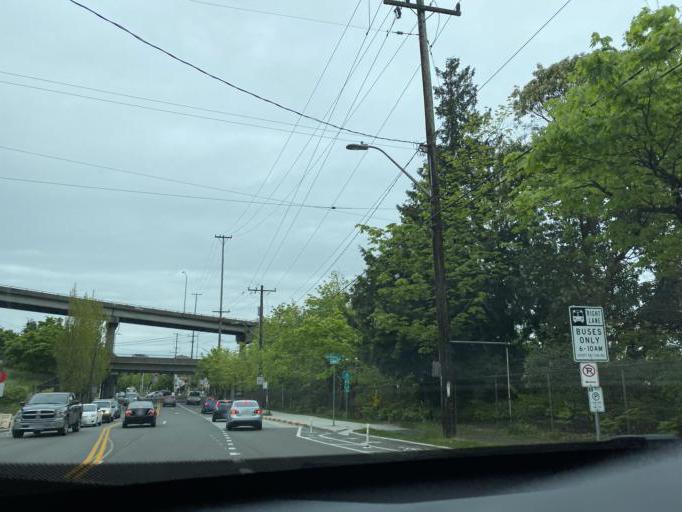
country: US
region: Washington
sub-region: King County
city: Seattle
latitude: 47.5703
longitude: -122.3706
